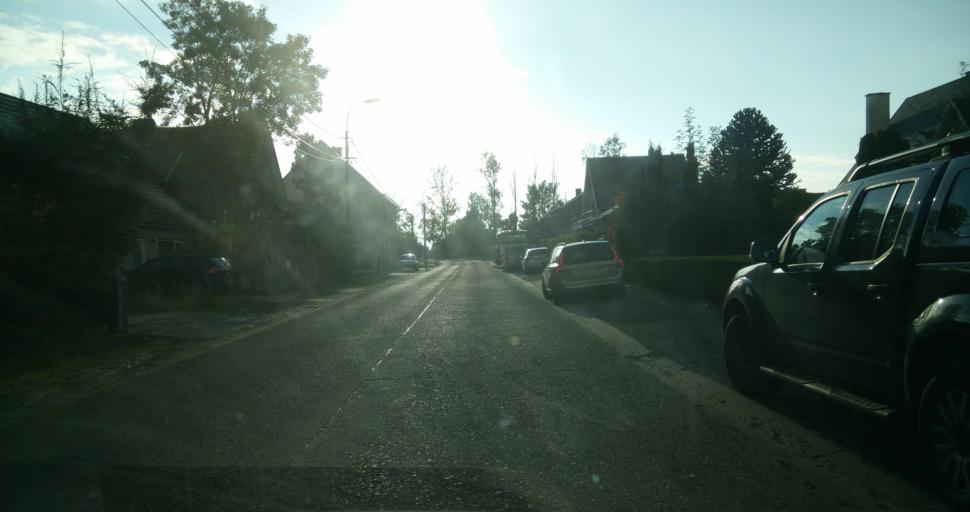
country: BE
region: Flanders
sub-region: Provincie Oost-Vlaanderen
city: Oosterzele
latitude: 50.9179
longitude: 3.7905
